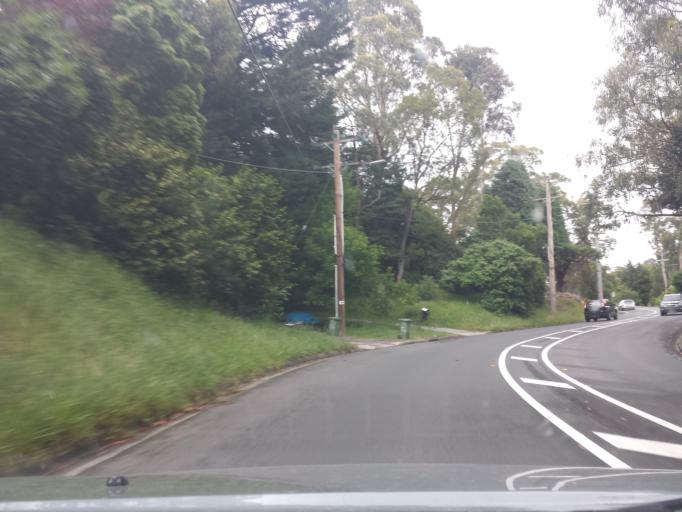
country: AU
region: Victoria
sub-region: Yarra Ranges
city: Belgrave Heights
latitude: -37.9134
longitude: 145.3439
